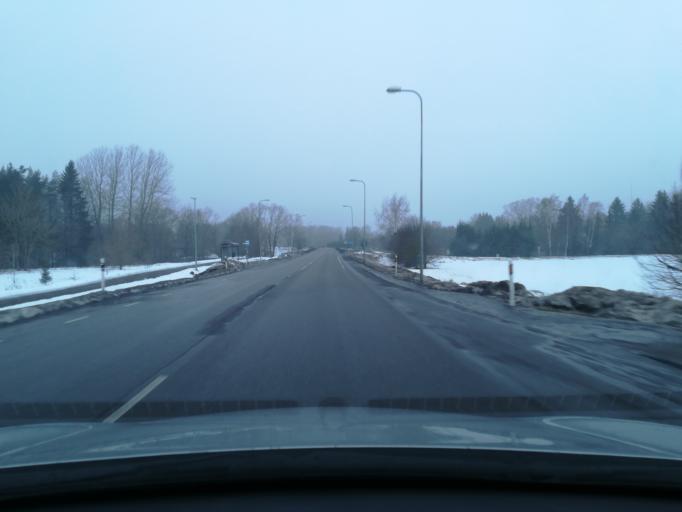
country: EE
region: Harju
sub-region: Rae vald
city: Jueri
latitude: 59.3612
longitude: 24.9502
